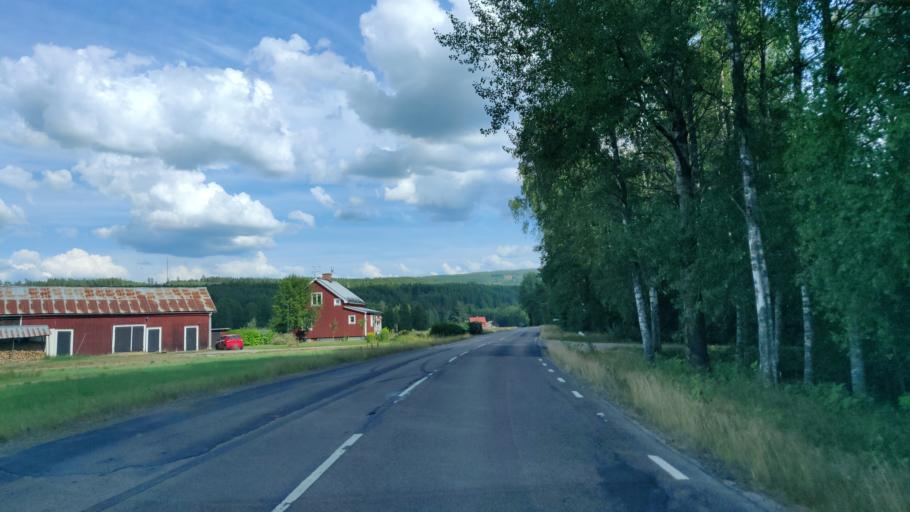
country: SE
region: Vaermland
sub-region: Hagfors Kommun
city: Ekshaerad
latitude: 60.1782
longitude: 13.5158
